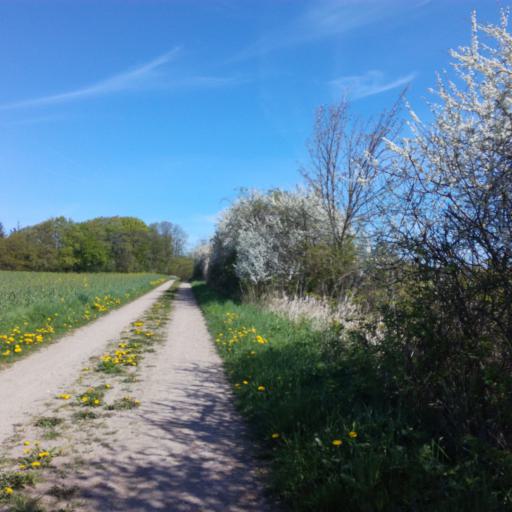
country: DK
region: South Denmark
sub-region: Vejle Kommune
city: Borkop
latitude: 55.6261
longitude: 9.6564
